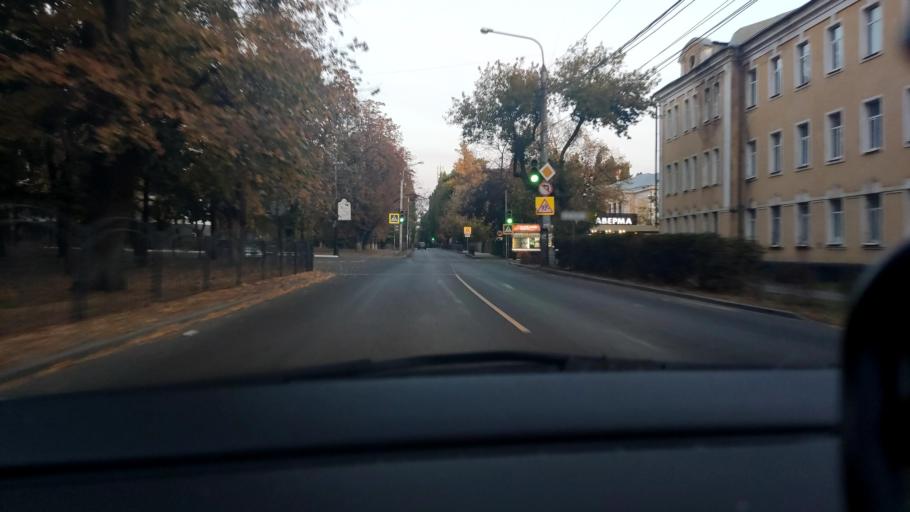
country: RU
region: Voronezj
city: Voronezh
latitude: 51.7125
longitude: 39.2291
